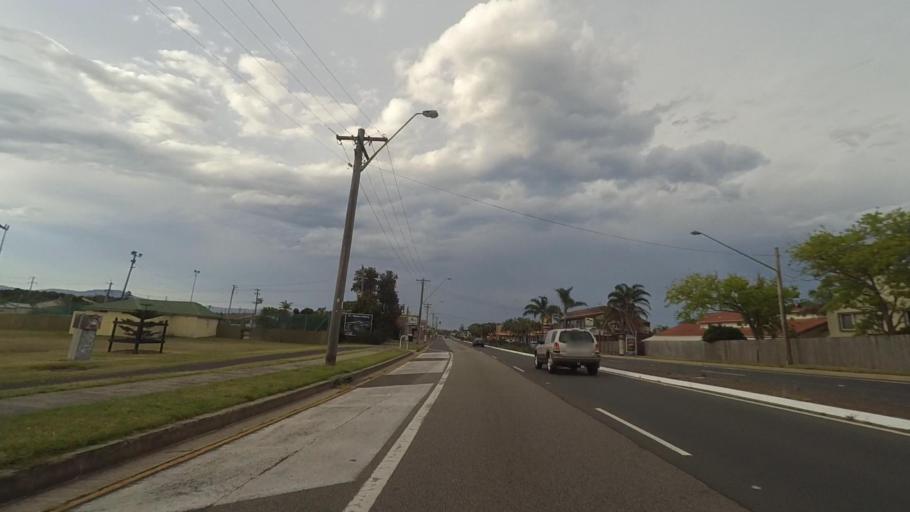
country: AU
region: New South Wales
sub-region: Shellharbour
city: Lake Illawarra
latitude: -34.5339
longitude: 150.8682
